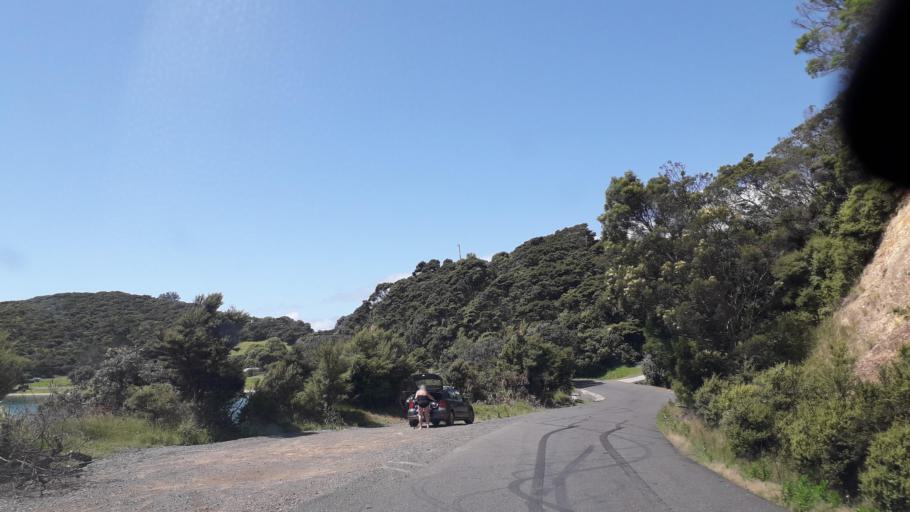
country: NZ
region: Northland
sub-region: Far North District
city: Paihia
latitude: -35.2285
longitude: 174.2627
